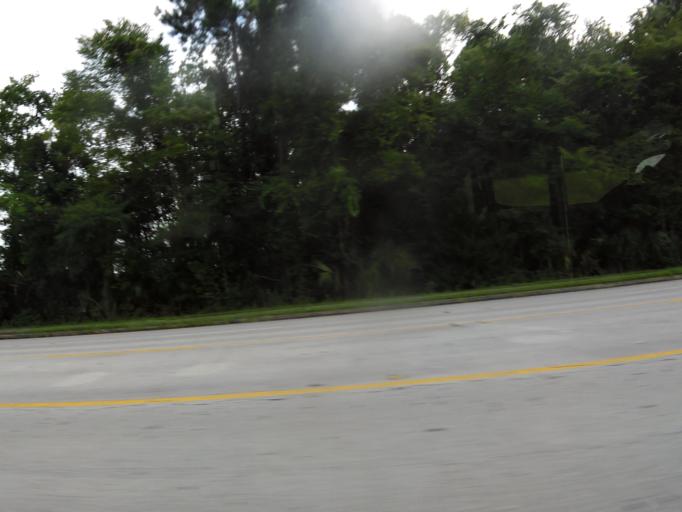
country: US
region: Florida
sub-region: Duval County
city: Jacksonville
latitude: 30.3384
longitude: -81.7703
